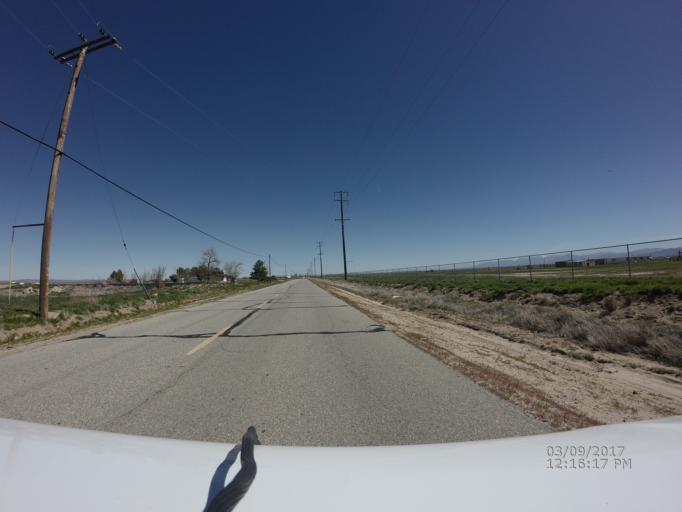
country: US
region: California
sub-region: Los Angeles County
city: Quartz Hill
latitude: 34.7330
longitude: -118.2634
